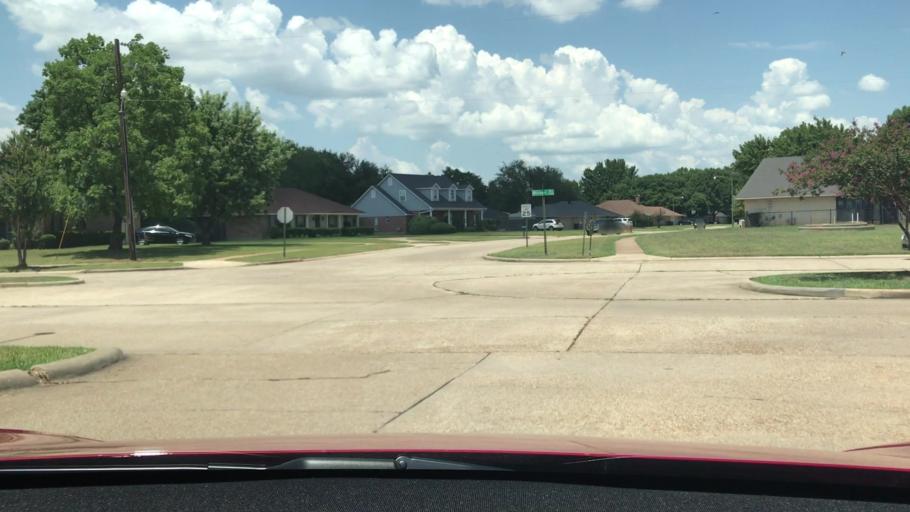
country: US
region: Louisiana
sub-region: Bossier Parish
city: Bossier City
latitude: 32.4278
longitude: -93.7189
